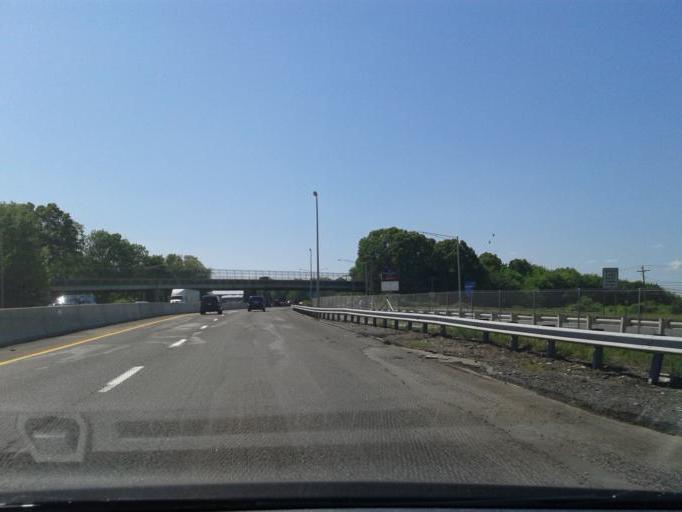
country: US
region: Connecticut
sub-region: New London County
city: New London
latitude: 41.3703
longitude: -72.1202
